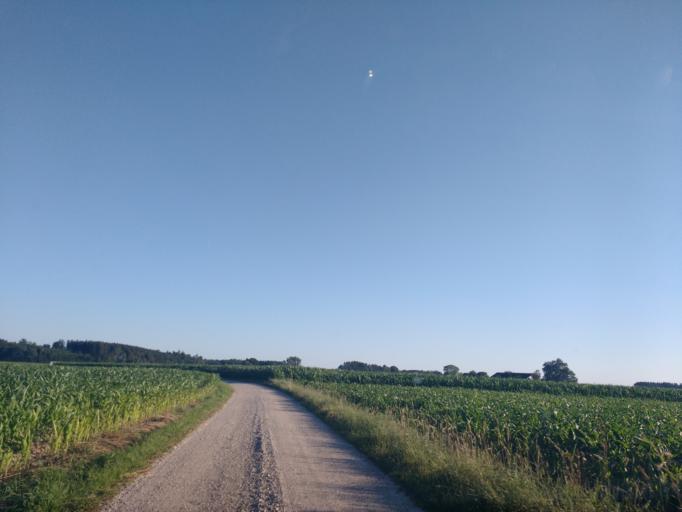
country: DE
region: Bavaria
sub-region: Upper Bavaria
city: Taufkirchen
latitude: 48.1416
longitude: 12.4694
